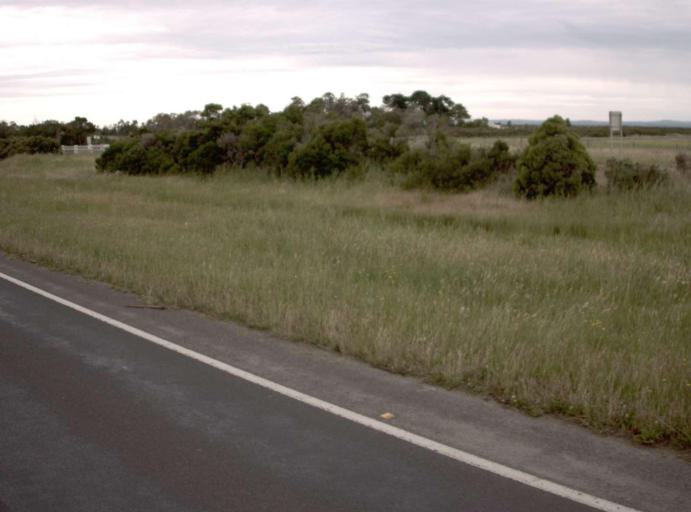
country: AU
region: Victoria
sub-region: Casey
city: Tooradin
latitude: -38.2120
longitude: 145.4260
